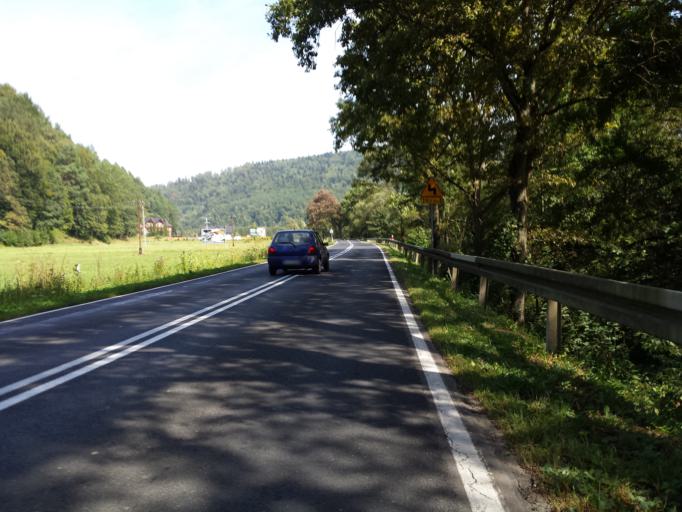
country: PL
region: Subcarpathian Voivodeship
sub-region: Powiat leski
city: Lesko
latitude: 49.4373
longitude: 22.3442
